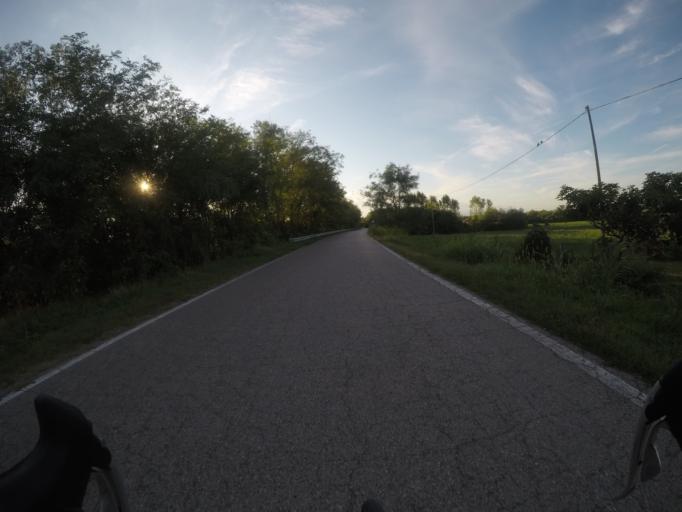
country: IT
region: Veneto
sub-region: Provincia di Rovigo
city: Castelguglielmo
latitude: 45.0170
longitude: 11.5646
